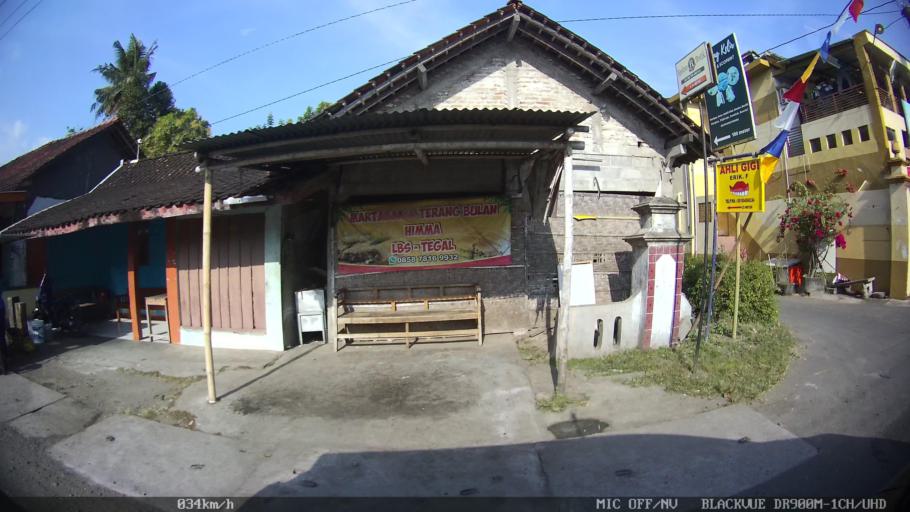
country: ID
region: Daerah Istimewa Yogyakarta
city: Pandak
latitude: -7.8962
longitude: 110.2983
